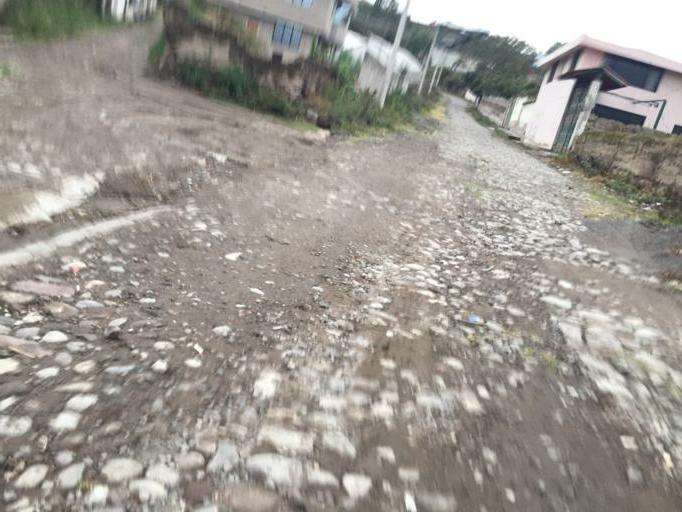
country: EC
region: Imbabura
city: Atuntaqui
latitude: 0.3408
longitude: -78.1730
